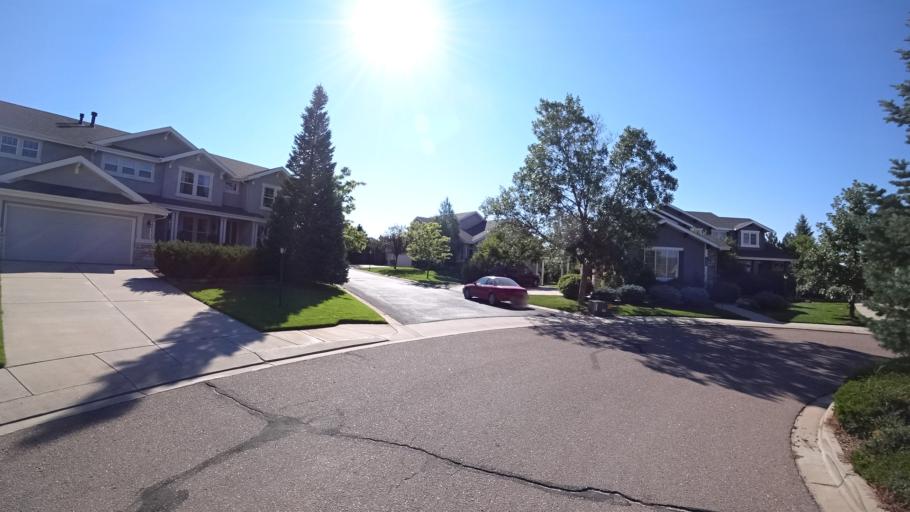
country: US
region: Colorado
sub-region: El Paso County
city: Black Forest
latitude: 38.9780
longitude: -104.7675
